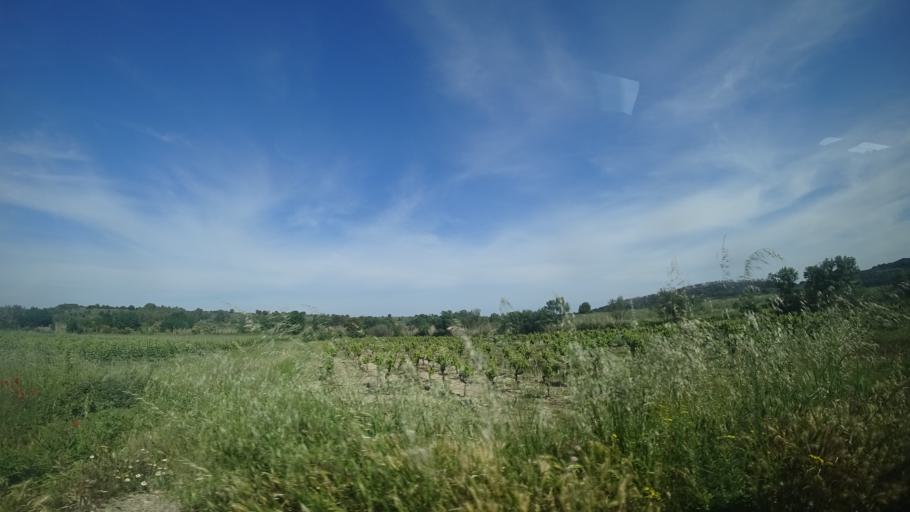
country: FR
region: Languedoc-Roussillon
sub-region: Departement de l'Aude
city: Ginestas
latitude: 43.2739
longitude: 2.8148
